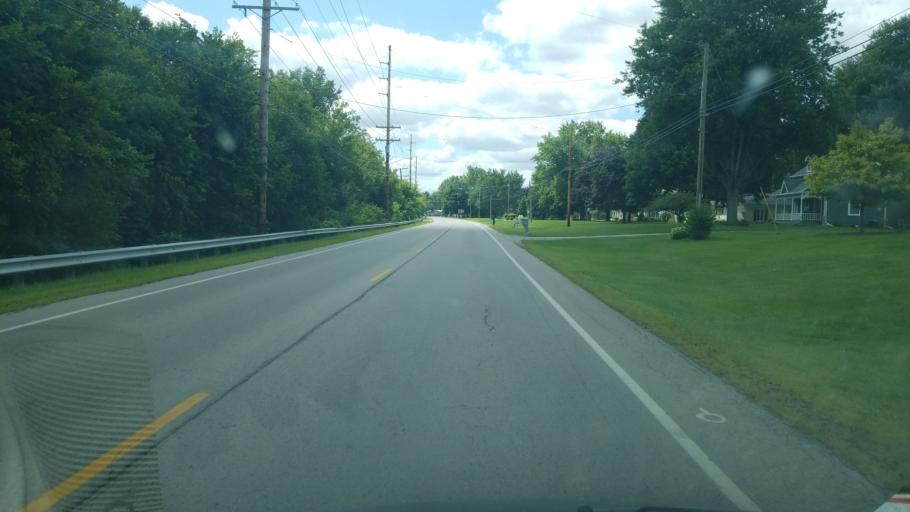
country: US
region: Ohio
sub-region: Henry County
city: Napoleon
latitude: 41.4081
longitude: -84.1007
